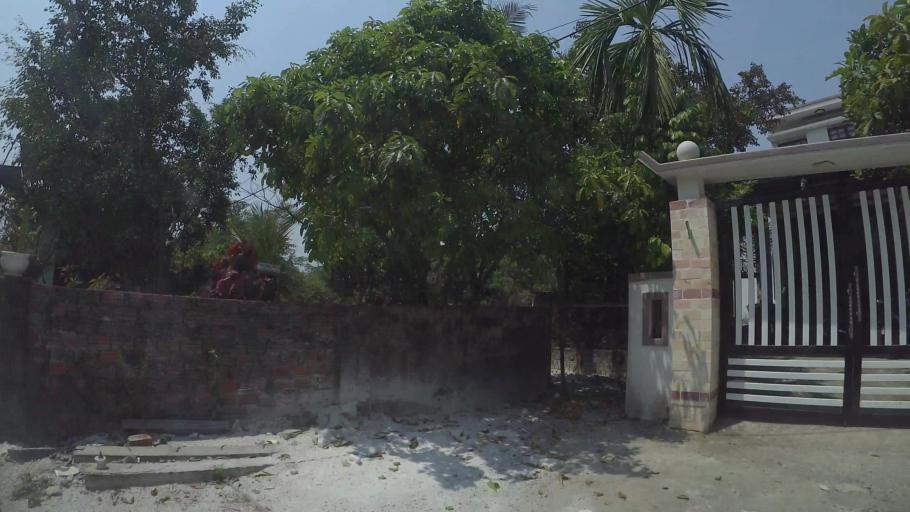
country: VN
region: Da Nang
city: Ngu Hanh Son
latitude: 15.9866
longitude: 108.2550
